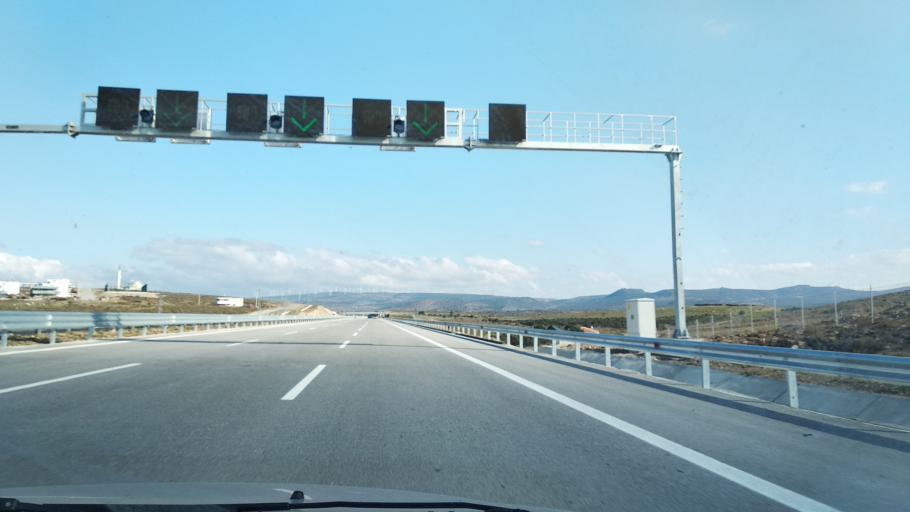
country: TR
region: Izmir
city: Yenisakran
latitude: 38.8542
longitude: 27.0590
